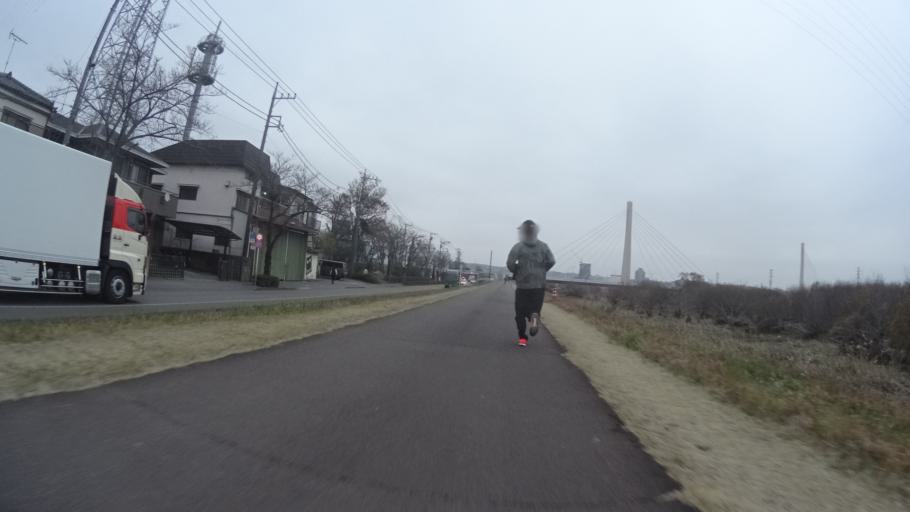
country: JP
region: Tokyo
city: Hino
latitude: 35.6633
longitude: 139.4388
